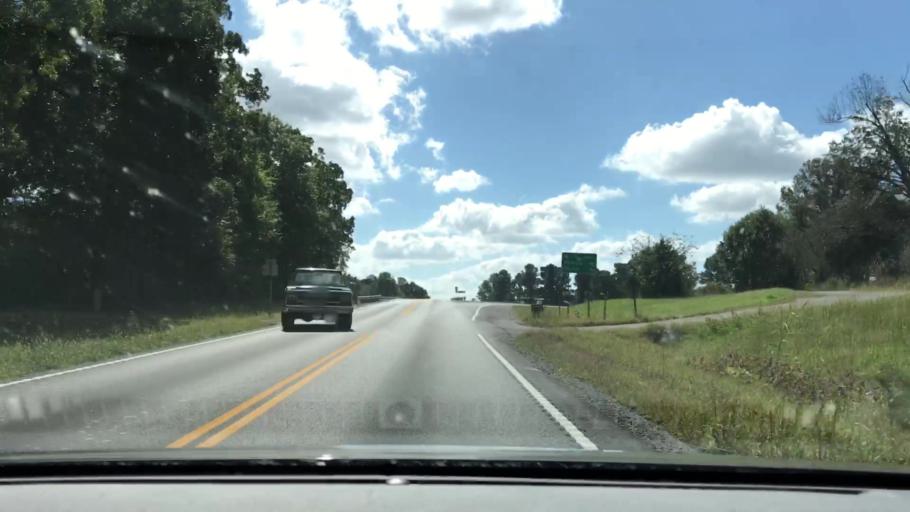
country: US
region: Kentucky
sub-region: Graves County
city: Mayfield
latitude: 36.7778
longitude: -88.5959
